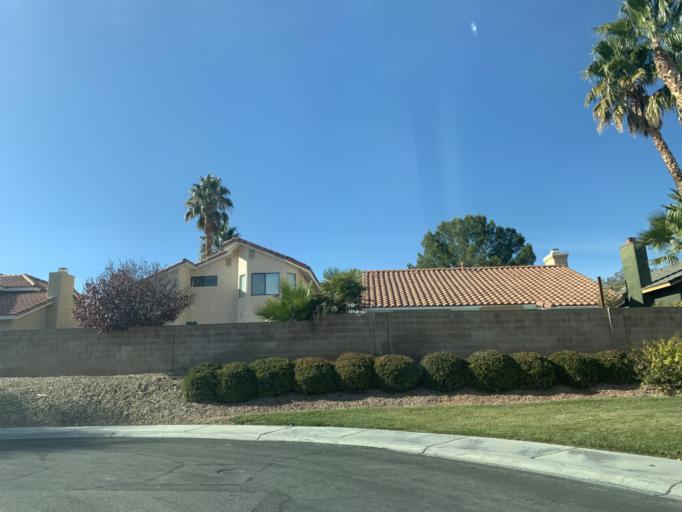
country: US
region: Nevada
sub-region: Clark County
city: Summerlin South
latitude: 36.1346
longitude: -115.2946
